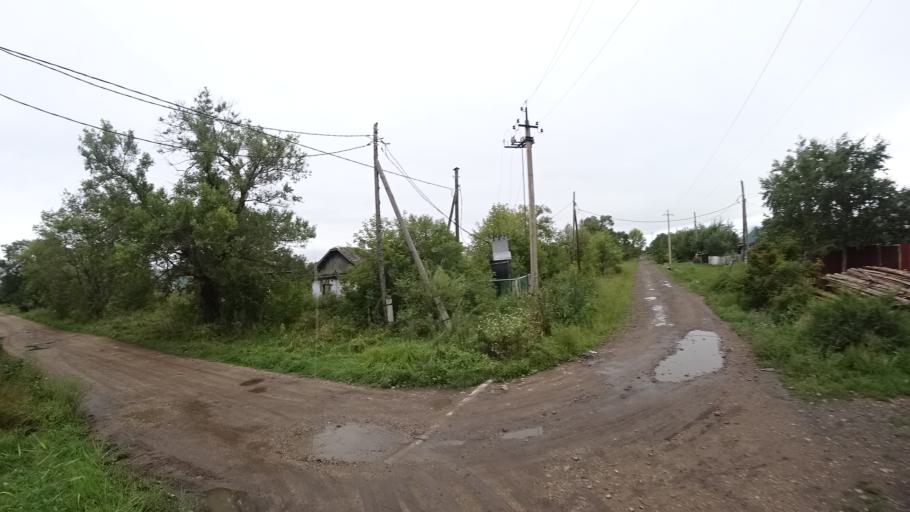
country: RU
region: Primorskiy
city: Chernigovka
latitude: 44.3446
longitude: 132.5325
